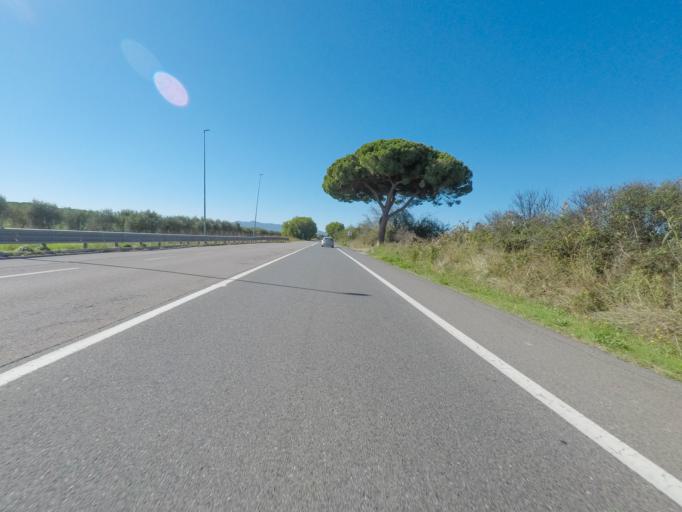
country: IT
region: Tuscany
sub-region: Provincia di Grosseto
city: Capalbio
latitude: 42.4151
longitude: 11.3645
